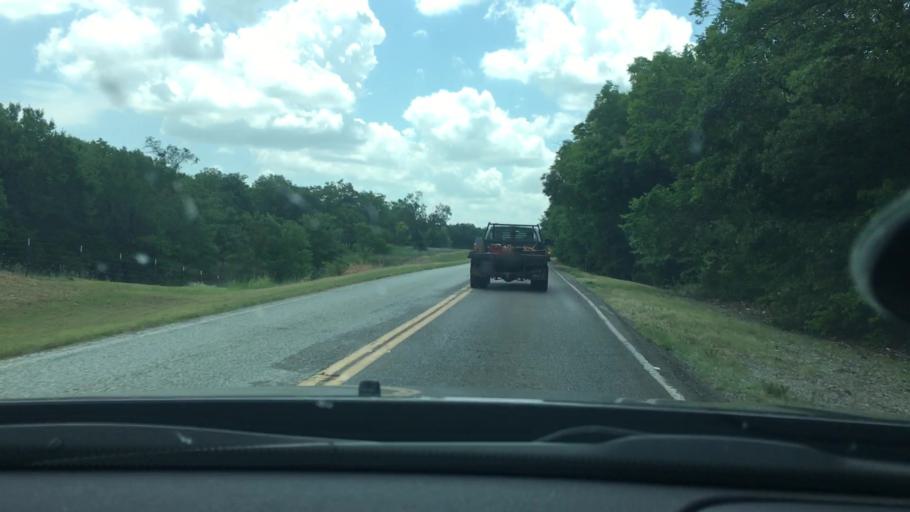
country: US
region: Oklahoma
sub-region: Pontotoc County
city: Ada
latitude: 34.5774
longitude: -96.6321
